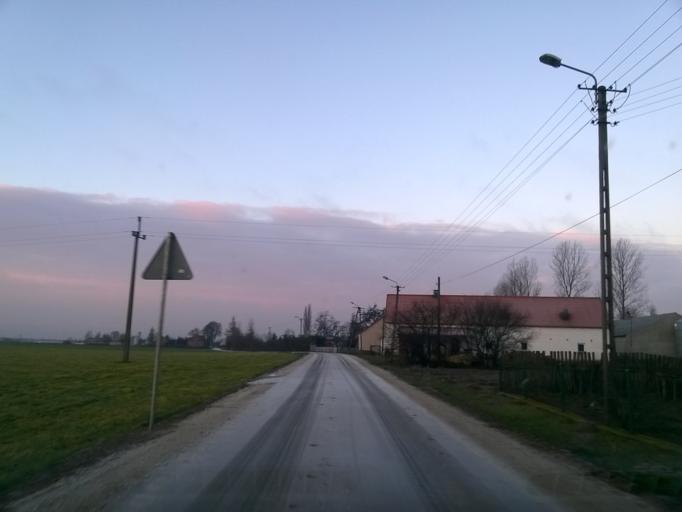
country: PL
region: Kujawsko-Pomorskie
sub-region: Powiat nakielski
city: Kcynia
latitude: 53.0148
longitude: 17.4463
